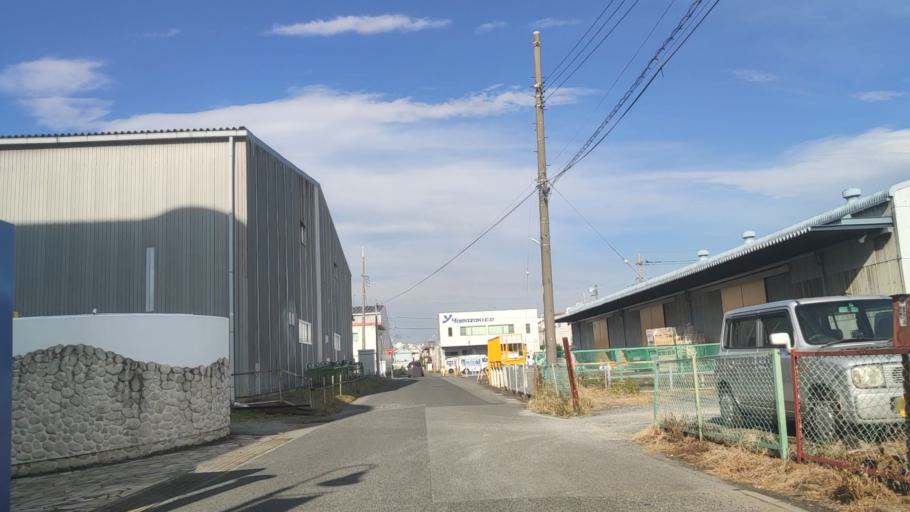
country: JP
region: Kanagawa
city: Atsugi
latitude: 35.4251
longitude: 139.3599
